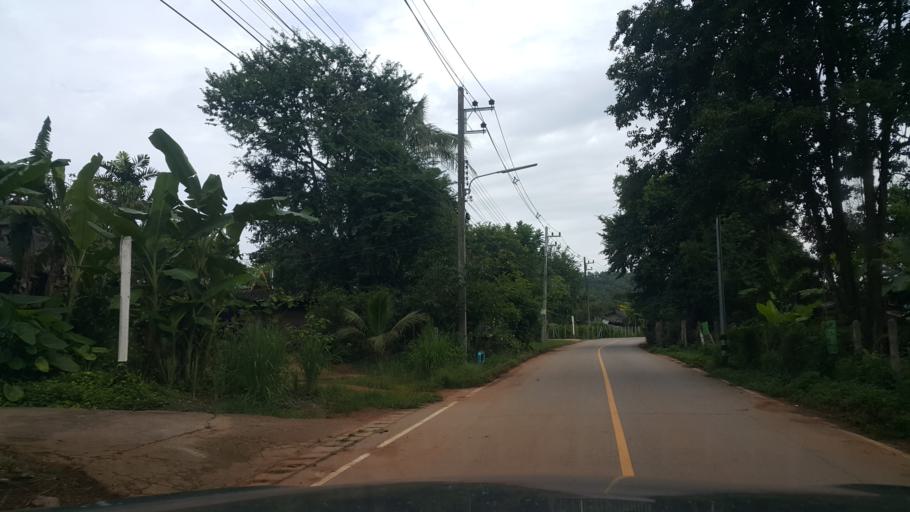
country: TH
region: Chiang Mai
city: San Sai
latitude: 18.9902
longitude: 99.1281
